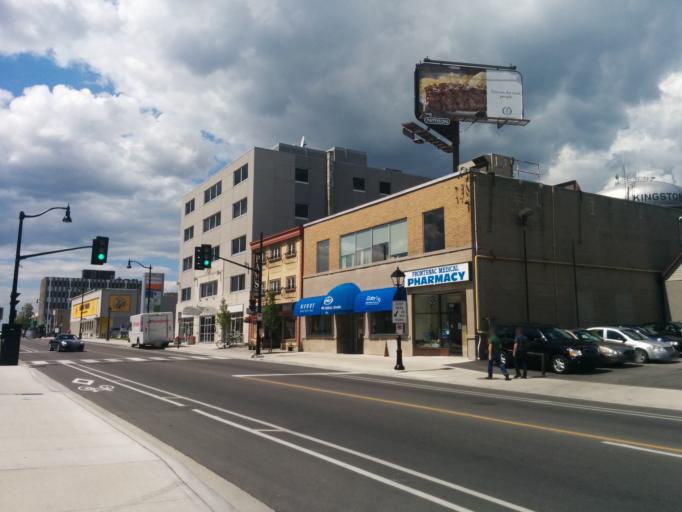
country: CA
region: Ontario
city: Kingston
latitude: 44.2390
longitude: -76.5067
